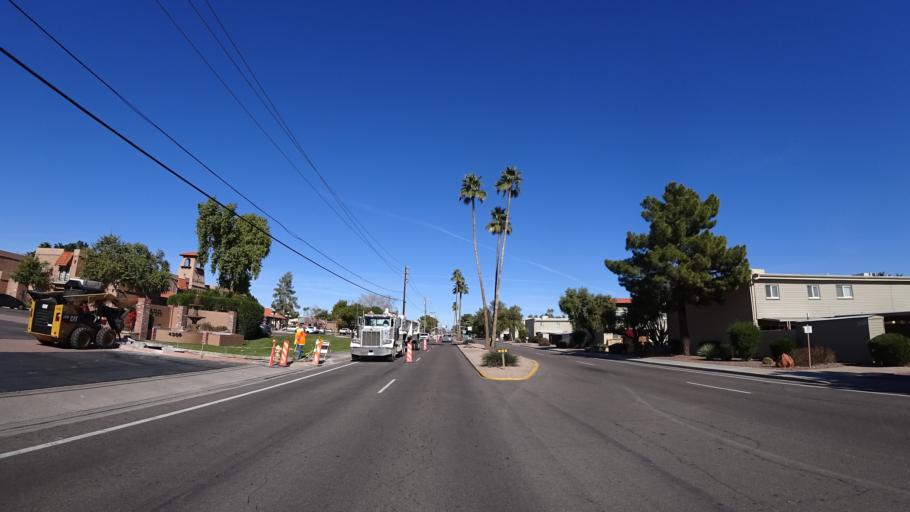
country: US
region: Arizona
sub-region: Maricopa County
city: Scottsdale
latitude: 33.4975
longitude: -111.9176
